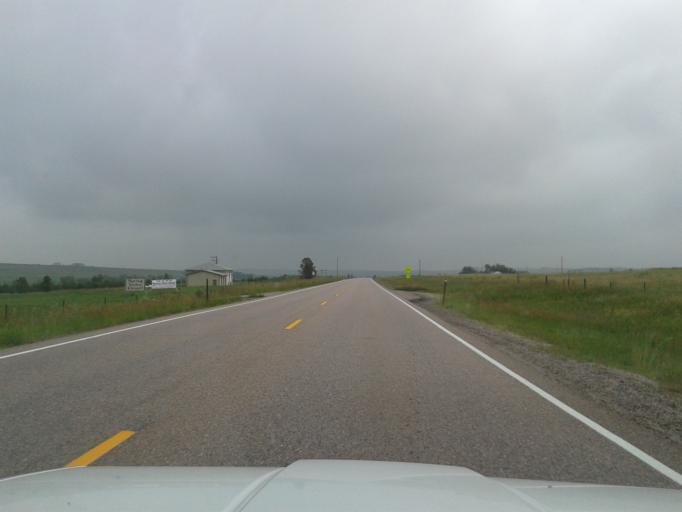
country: US
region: Colorado
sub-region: El Paso County
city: Woodmoor
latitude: 39.2063
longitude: -104.7149
